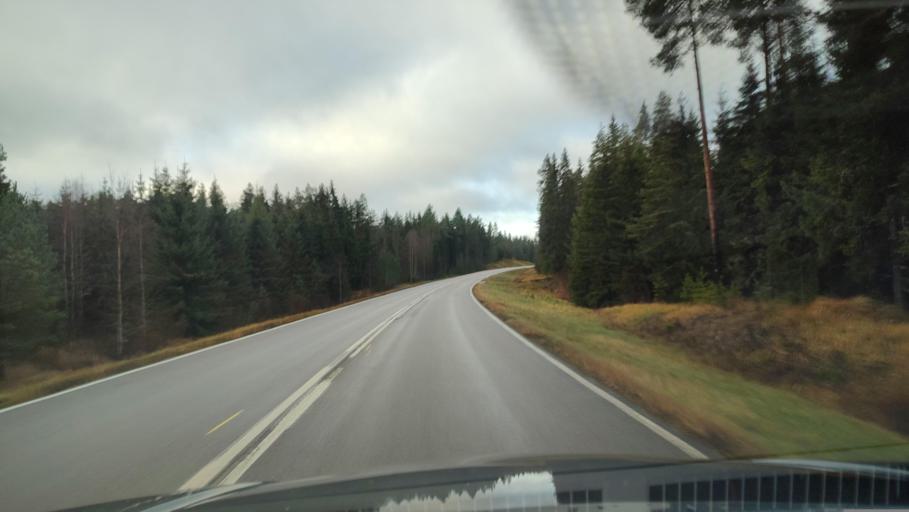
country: FI
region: Ostrobothnia
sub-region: Sydosterbotten
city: Kristinestad
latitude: 62.3045
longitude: 21.4389
